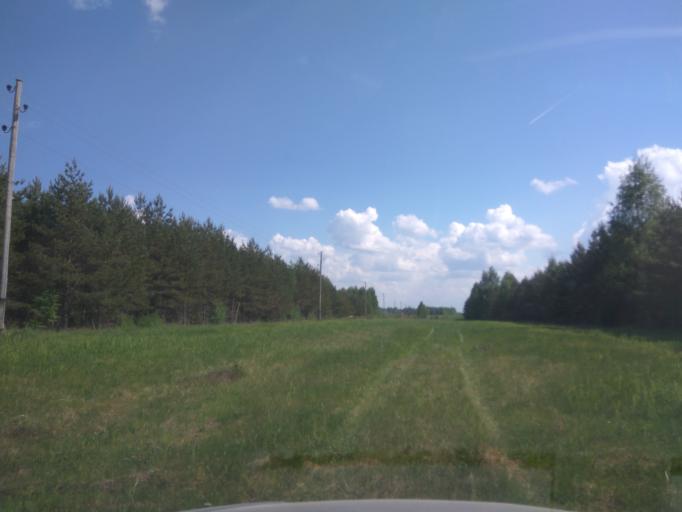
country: LV
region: Kuldigas Rajons
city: Kuldiga
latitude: 57.1807
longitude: 22.0028
